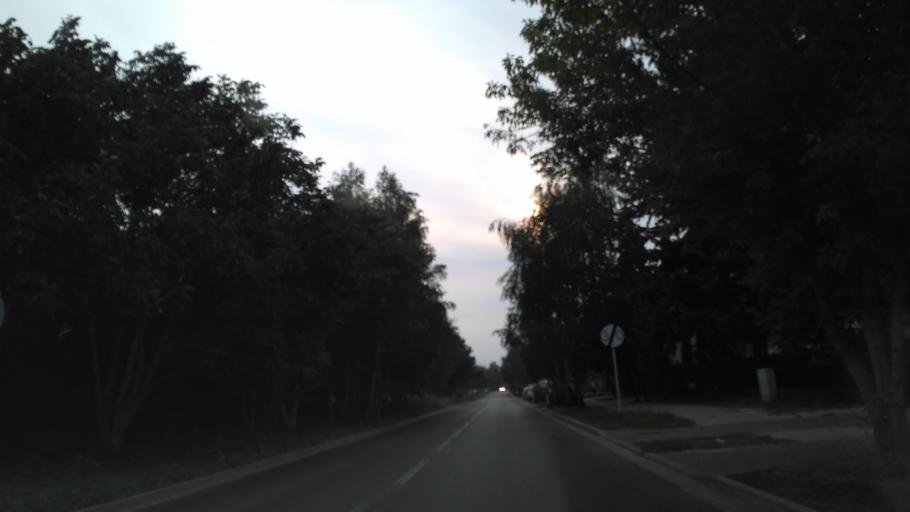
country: PL
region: Lublin Voivodeship
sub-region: Powiat lubelski
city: Lublin
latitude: 51.2255
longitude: 22.5939
